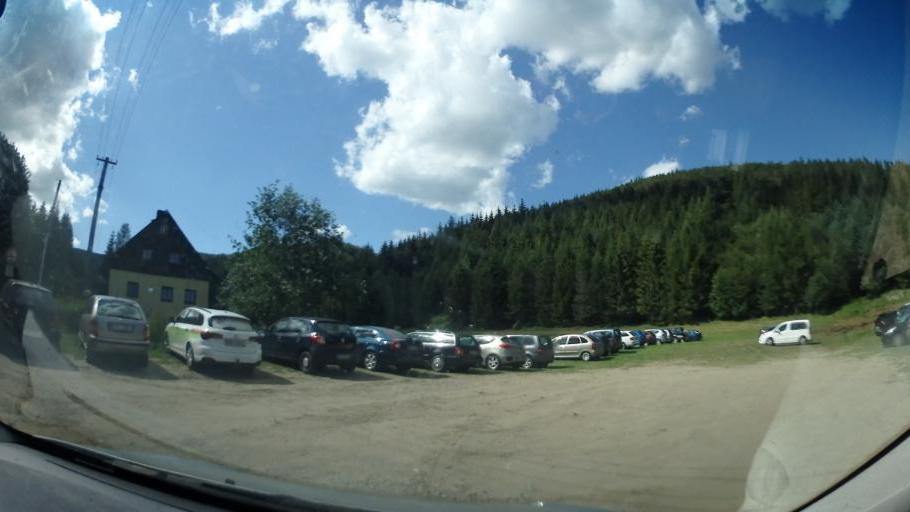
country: CZ
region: Olomoucky
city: Vapenna
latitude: 50.2252
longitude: 17.0784
